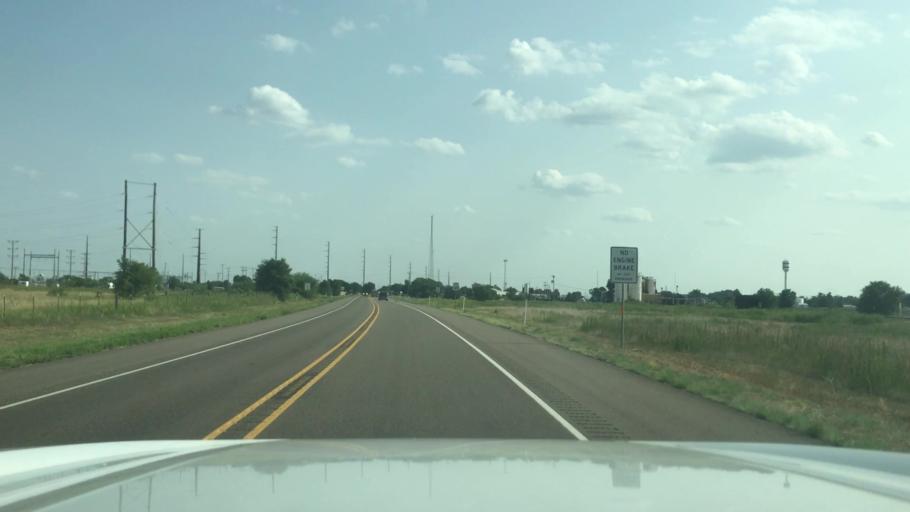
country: US
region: Texas
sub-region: Hartley County
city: Channing
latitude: 35.6936
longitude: -102.3282
